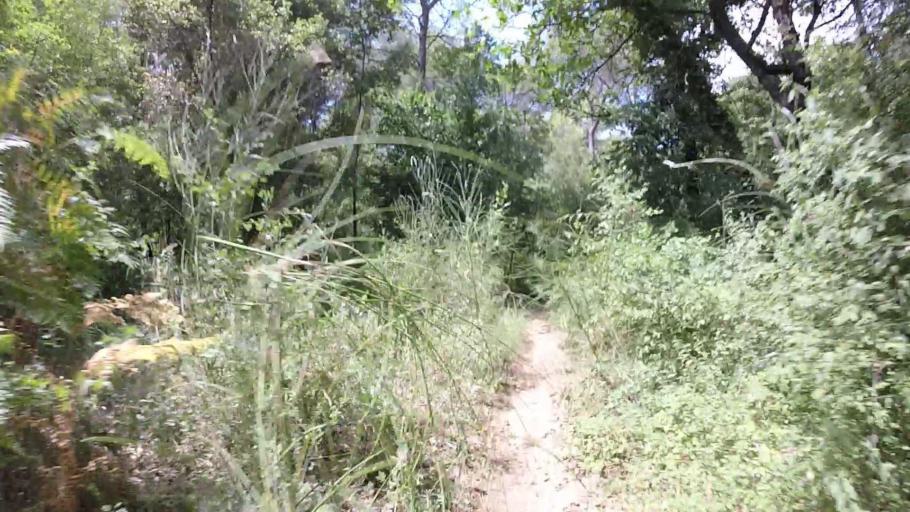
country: FR
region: Provence-Alpes-Cote d'Azur
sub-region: Departement des Alpes-Maritimes
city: Mougins
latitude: 43.6139
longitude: 7.0182
